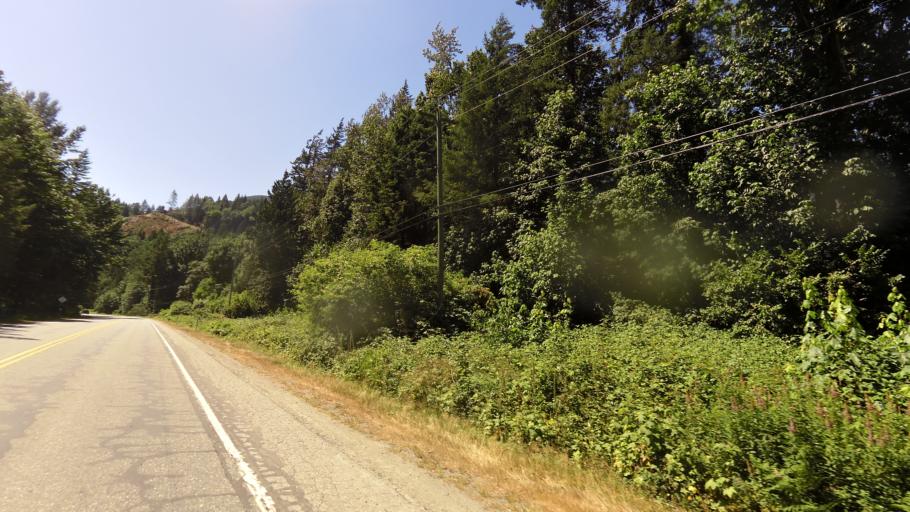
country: CA
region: British Columbia
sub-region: Fraser Valley Regional District
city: Chilliwack
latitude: 49.2309
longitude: -122.0123
